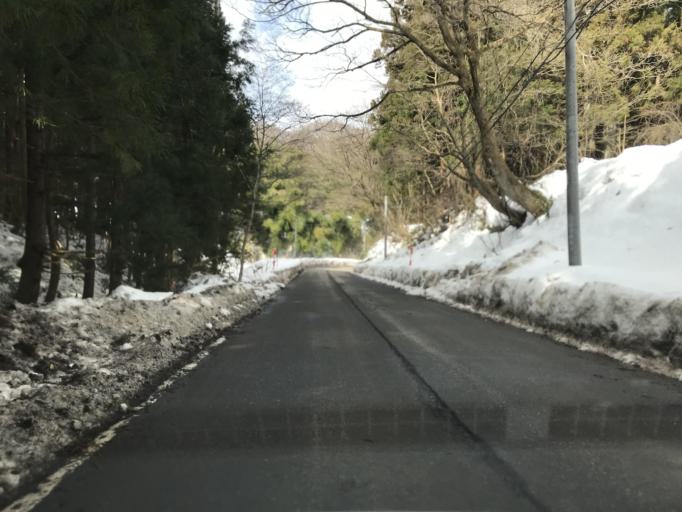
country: JP
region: Miyagi
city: Furukawa
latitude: 38.7242
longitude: 140.7612
